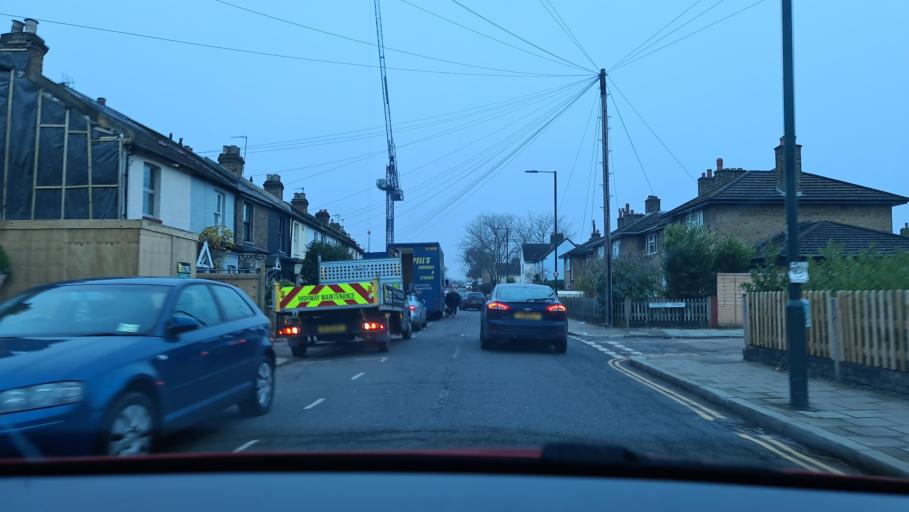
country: GB
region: England
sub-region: Greater London
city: Richmond
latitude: 51.4700
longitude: -0.2879
